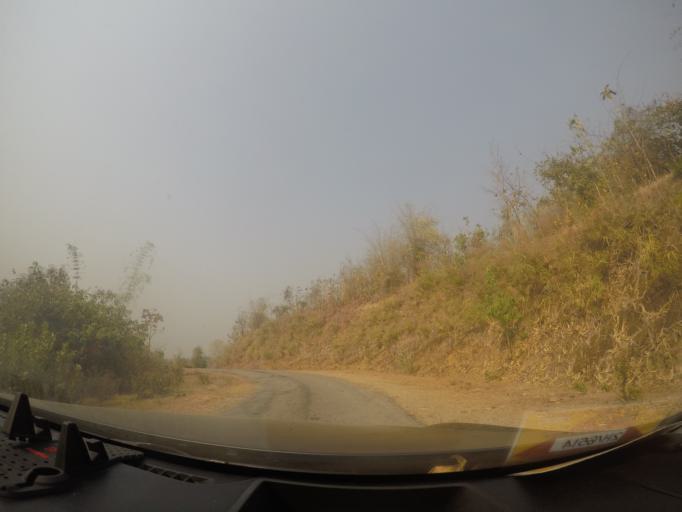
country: MM
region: Magway
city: Taungdwingyi
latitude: 19.9325
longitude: 95.8272
